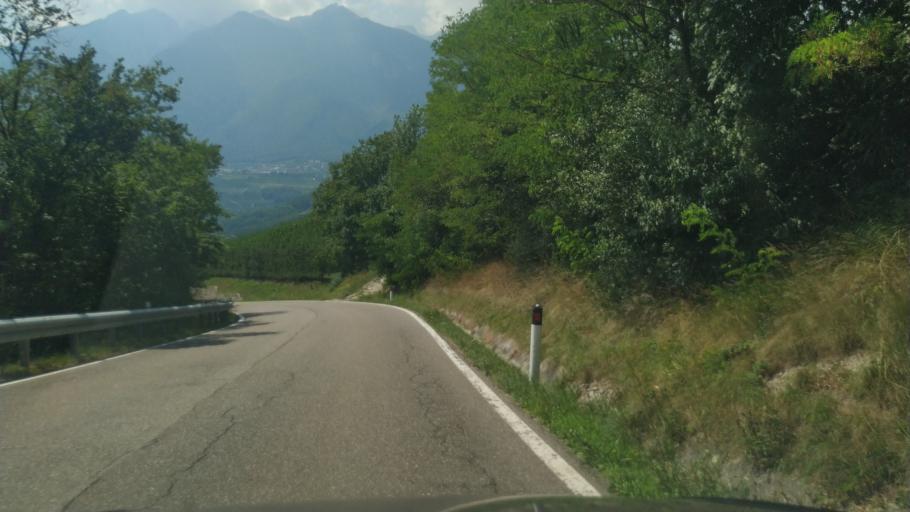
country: IT
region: Trentino-Alto Adige
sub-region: Provincia di Trento
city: Vigo di Ton
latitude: 46.2519
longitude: 11.0687
